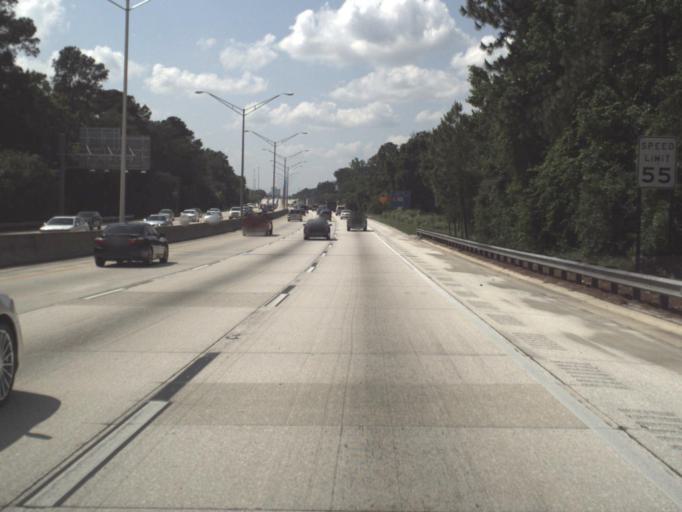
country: US
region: Florida
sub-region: Duval County
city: Jacksonville
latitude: 30.2838
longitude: -81.6224
